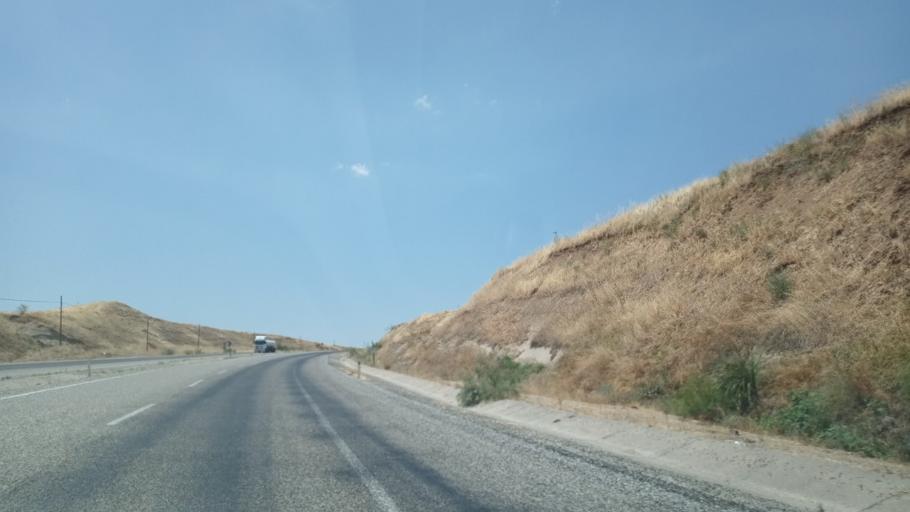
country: TR
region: Batman
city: Bekirhan
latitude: 38.1366
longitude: 41.2729
